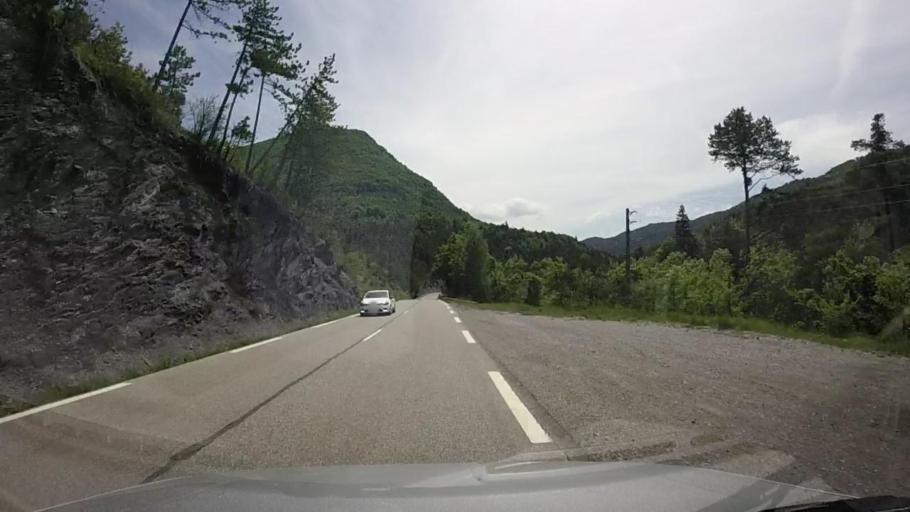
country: FR
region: Provence-Alpes-Cote d'Azur
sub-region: Departement des Alpes-de-Haute-Provence
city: Le Brusquet
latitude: 44.2276
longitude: 6.3620
